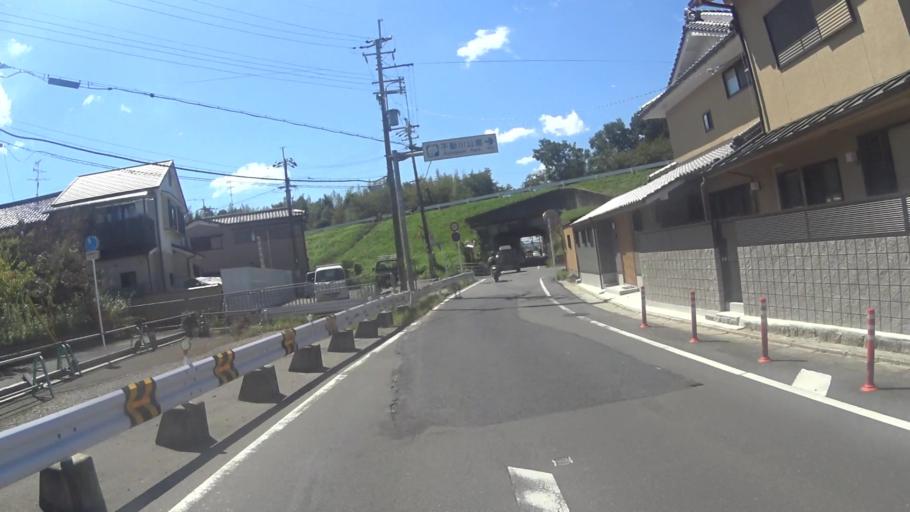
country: JP
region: Kyoto
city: Tanabe
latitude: 34.7806
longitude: 135.8131
